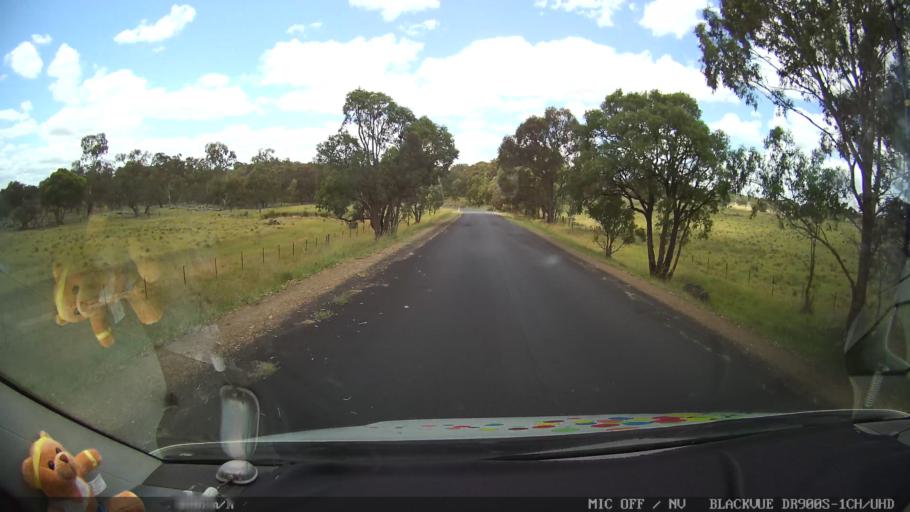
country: AU
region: New South Wales
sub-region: Glen Innes Severn
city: Glen Innes
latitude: -29.4300
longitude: 151.6661
